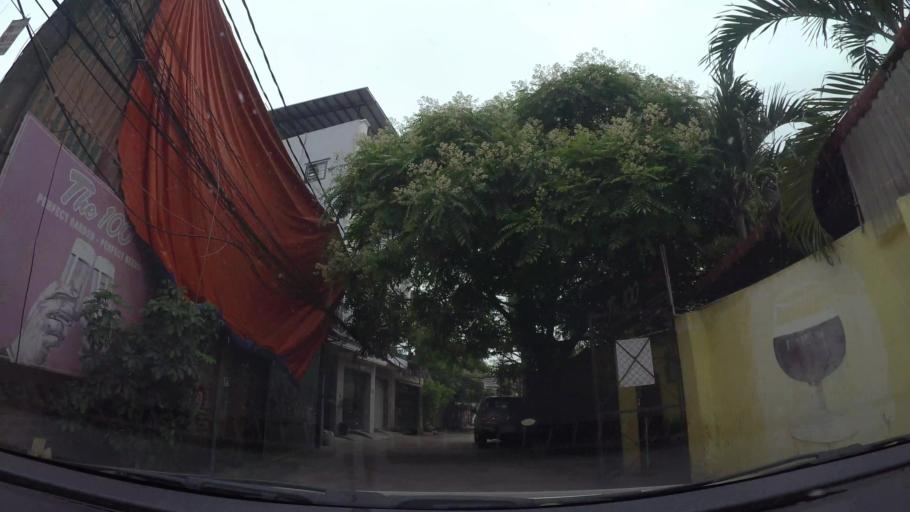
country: VN
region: Ha Noi
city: Tay Ho
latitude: 21.0689
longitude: 105.8297
